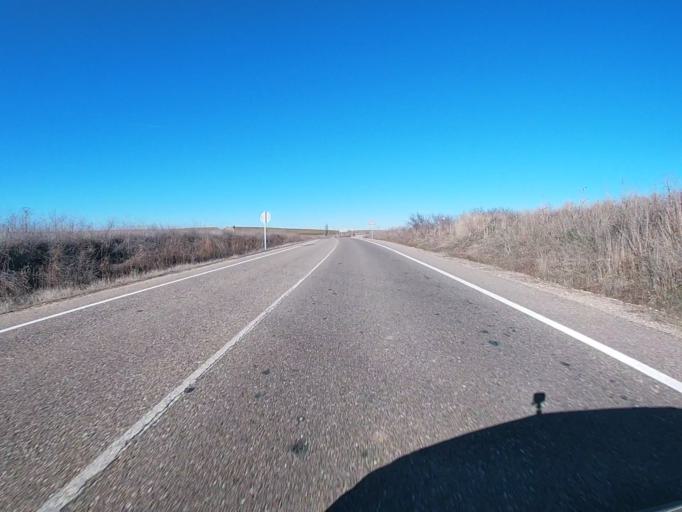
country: ES
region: Castille and Leon
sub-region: Provincia de Salamanca
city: Almenara de Tormes
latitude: 41.0662
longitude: -5.8254
